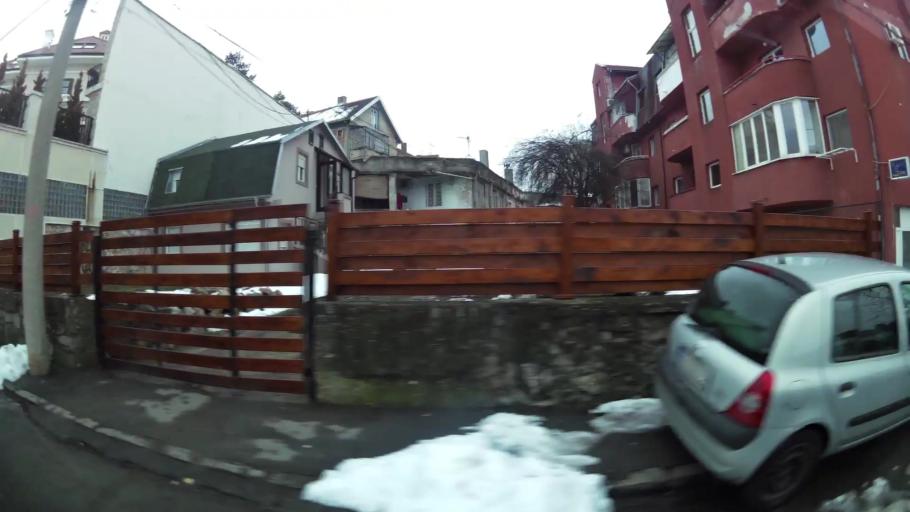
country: RS
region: Central Serbia
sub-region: Belgrade
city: Rakovica
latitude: 44.7570
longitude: 20.4500
